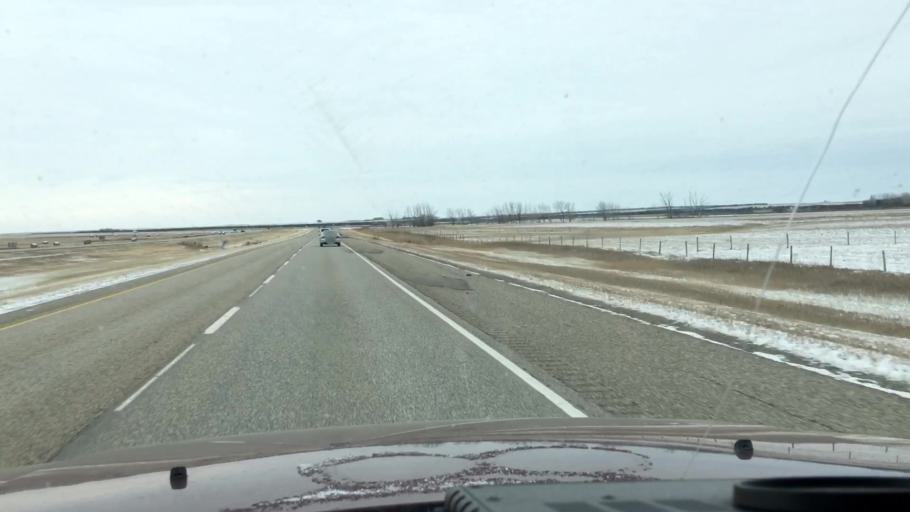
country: CA
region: Saskatchewan
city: Saskatoon
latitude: 51.4819
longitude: -106.2504
